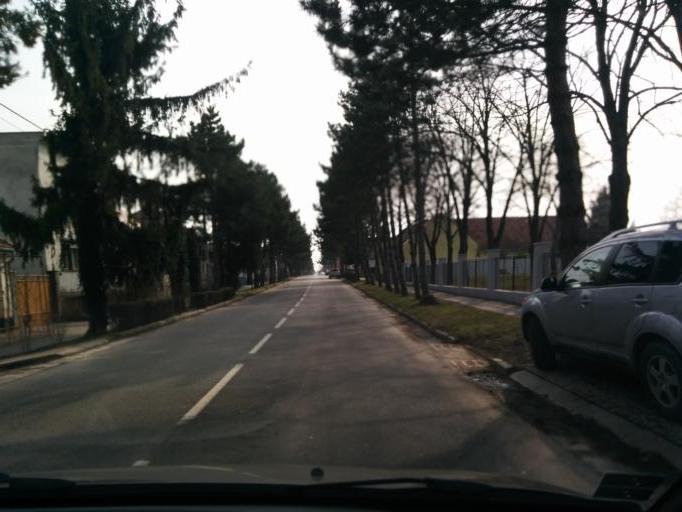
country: SK
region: Trnavsky
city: Sladkovicovo
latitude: 48.2463
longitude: 17.6200
